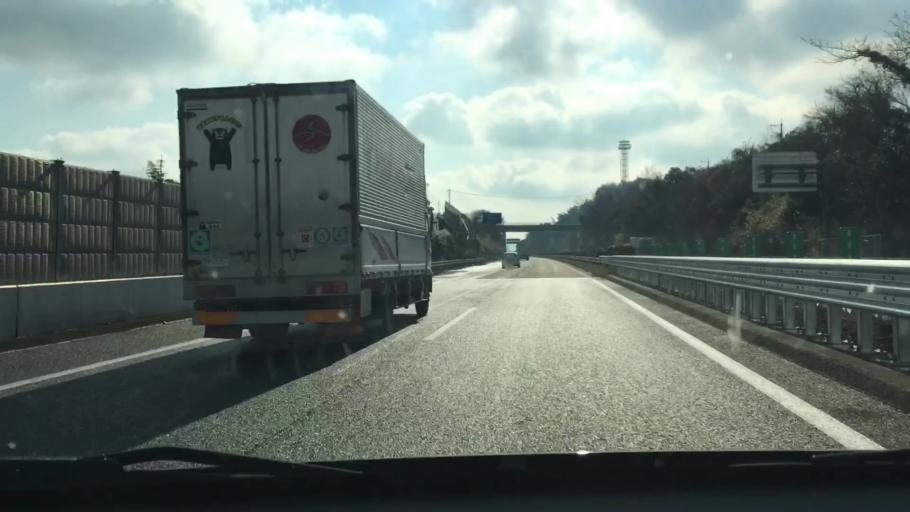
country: JP
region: Kumamoto
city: Kumamoto
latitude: 32.7303
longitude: 130.7748
